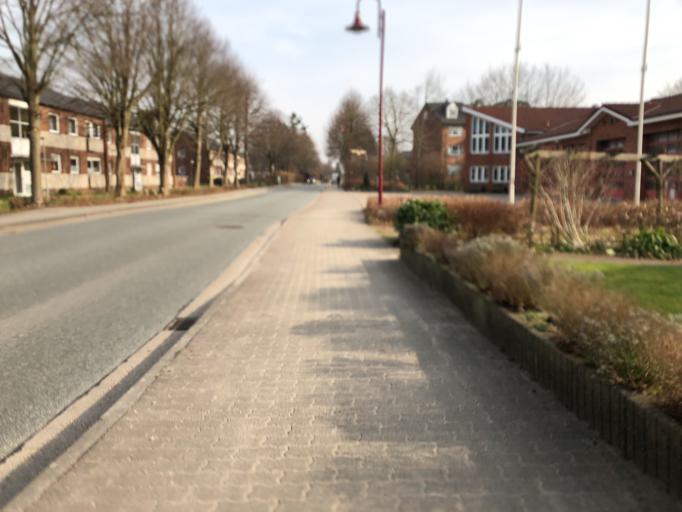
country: DE
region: Schleswig-Holstein
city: Tarp
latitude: 54.6648
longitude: 9.4065
